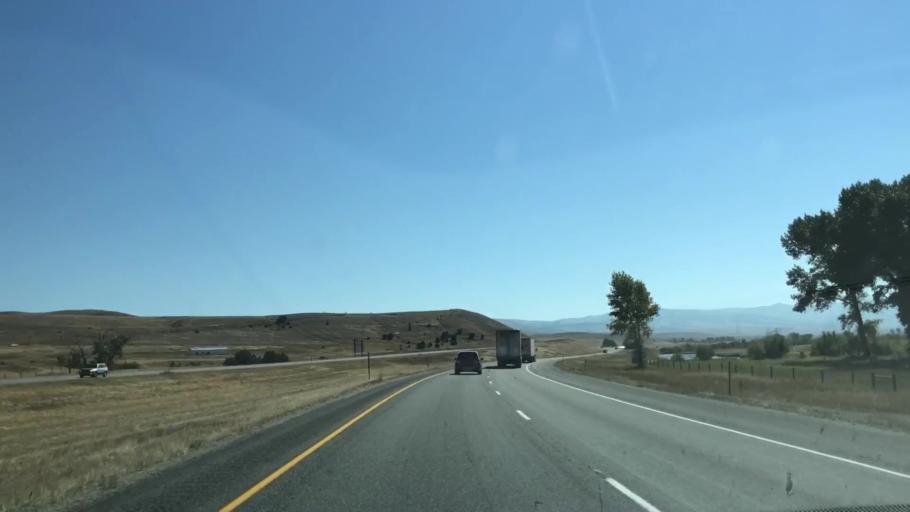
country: US
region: Montana
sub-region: Powell County
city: Deer Lodge
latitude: 46.5039
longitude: -112.7482
